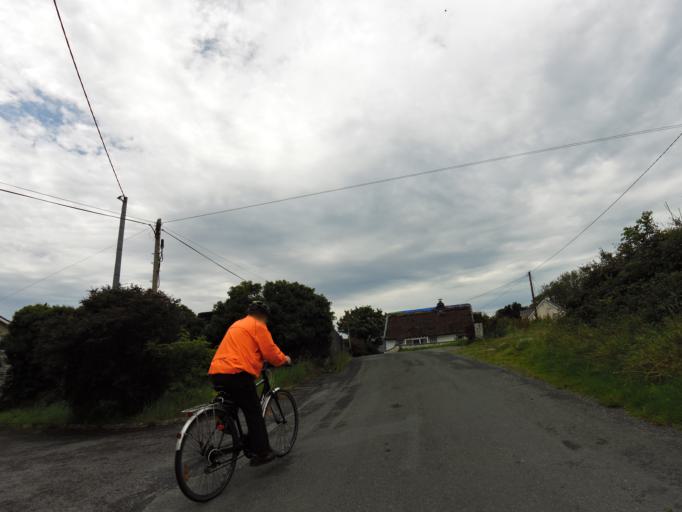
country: IE
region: Connaught
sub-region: County Galway
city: Gaillimh
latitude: 53.3024
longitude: -9.0736
